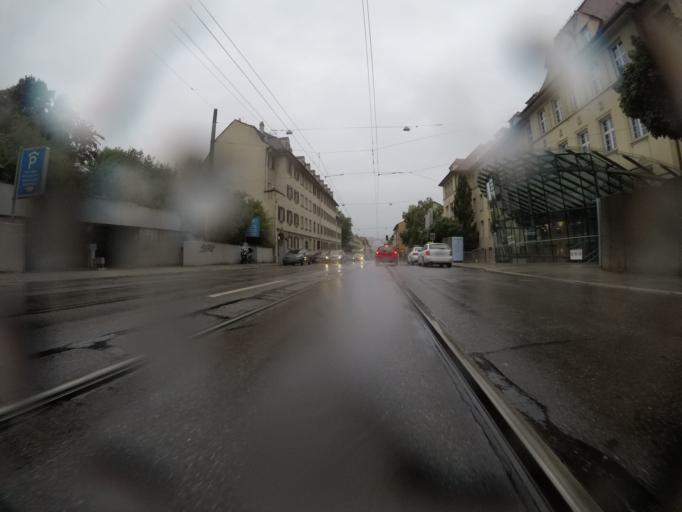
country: DE
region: Baden-Wuerttemberg
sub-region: Regierungsbezirk Stuttgart
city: Stuttgart-Ost
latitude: 48.7891
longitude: 9.2041
